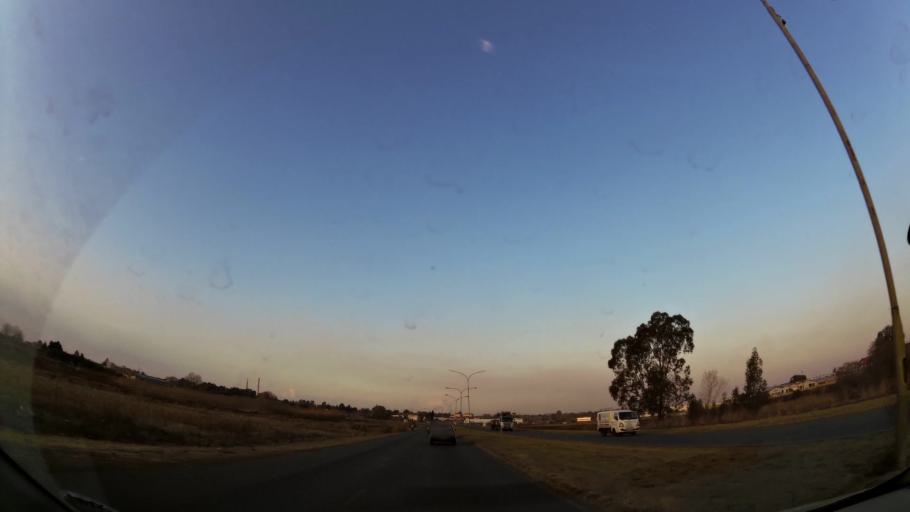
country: ZA
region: Gauteng
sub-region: Ekurhuleni Metropolitan Municipality
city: Springs
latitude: -26.2721
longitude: 28.3967
